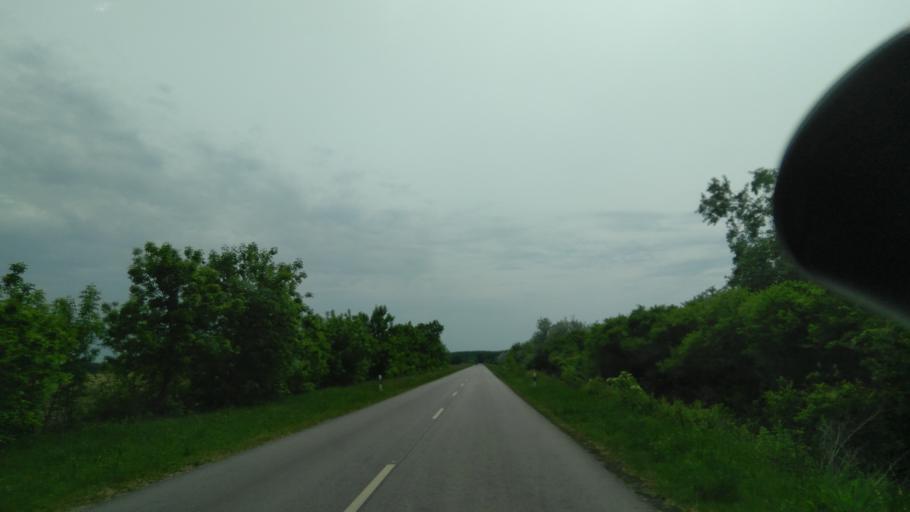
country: HU
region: Bekes
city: Mehkerek
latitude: 46.8319
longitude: 21.4240
